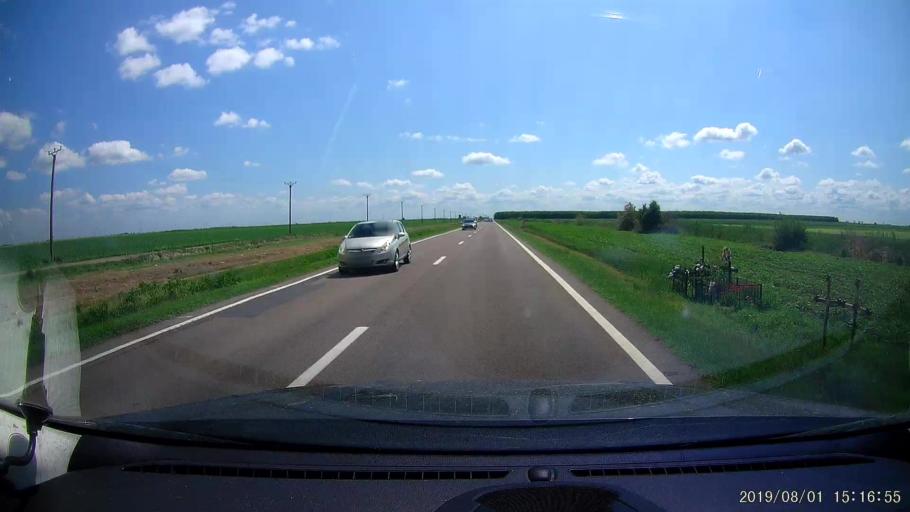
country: RO
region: Braila
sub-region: Comuna Unirea
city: Unirea
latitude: 45.1376
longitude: 27.8447
